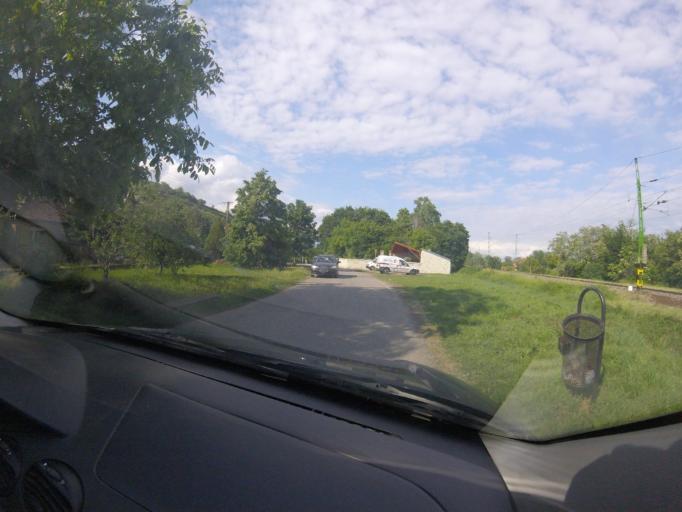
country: HU
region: Borsod-Abauj-Zemplen
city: Tokaj
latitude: 48.1141
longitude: 21.4081
